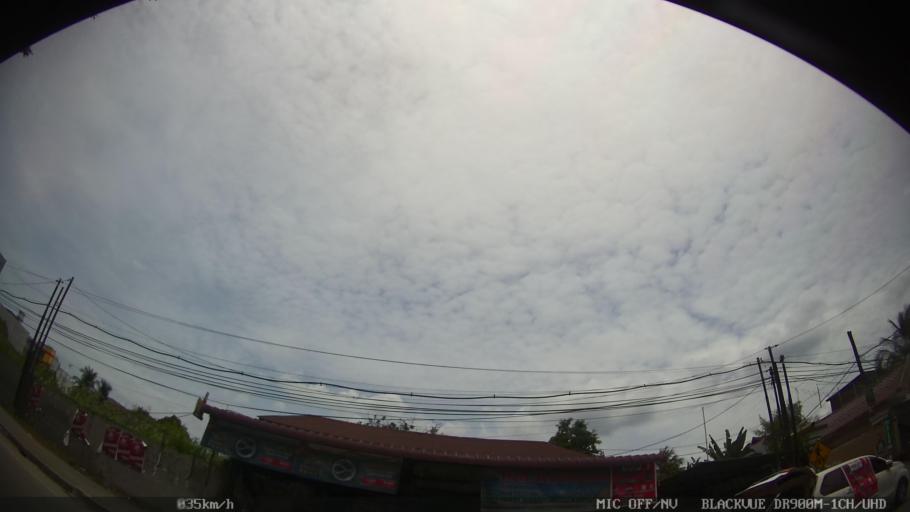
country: ID
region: North Sumatra
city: Deli Tua
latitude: 3.5308
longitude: 98.6415
